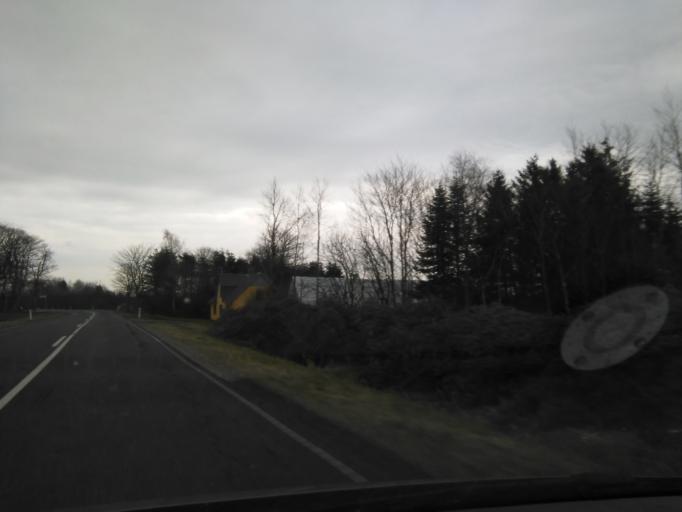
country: DK
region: North Denmark
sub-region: Mariagerfjord Kommune
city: Mariager
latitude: 56.6902
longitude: 9.9600
